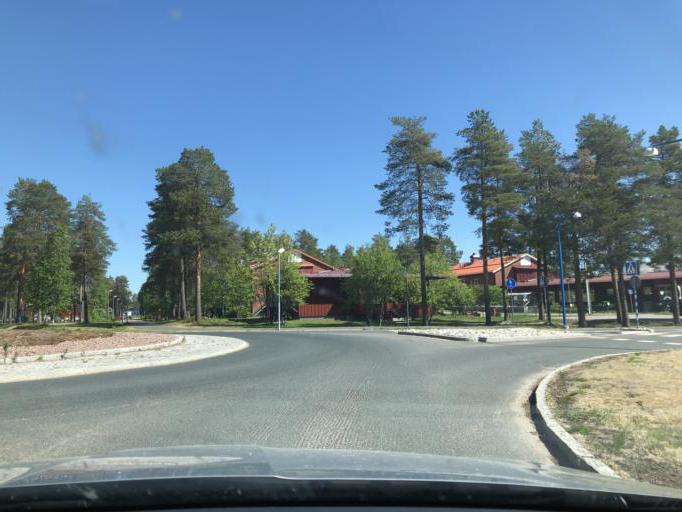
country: SE
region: Norrbotten
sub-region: Kalix Kommun
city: Kalix
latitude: 65.8539
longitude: 23.1610
